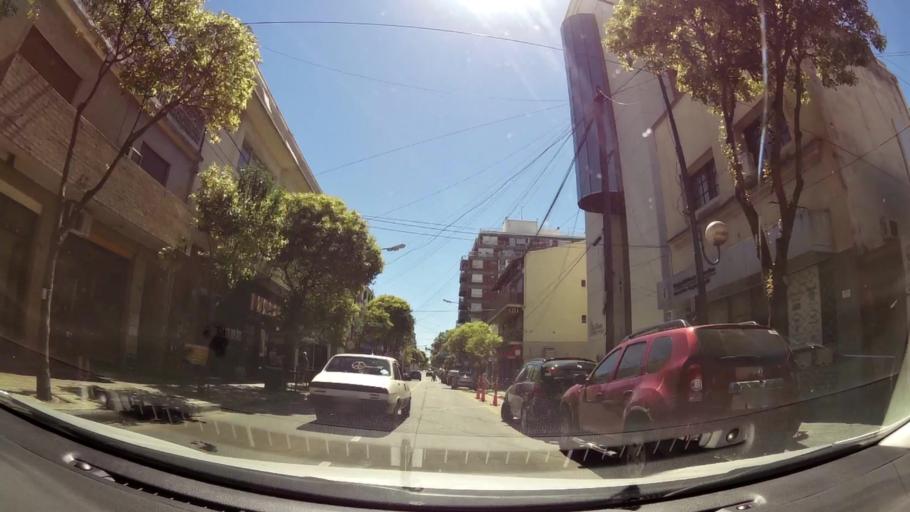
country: AR
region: Buenos Aires
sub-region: Partido de Vicente Lopez
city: Olivos
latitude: -34.5279
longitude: -58.4919
